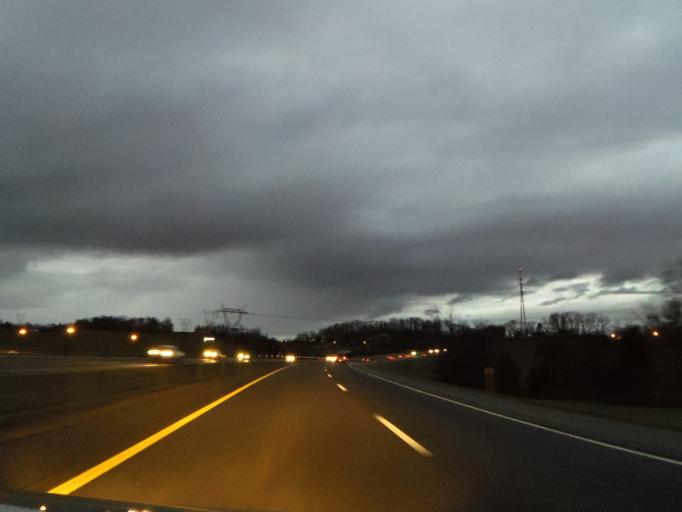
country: US
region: Tennessee
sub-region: Washington County
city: Gray
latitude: 36.4251
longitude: -82.5122
